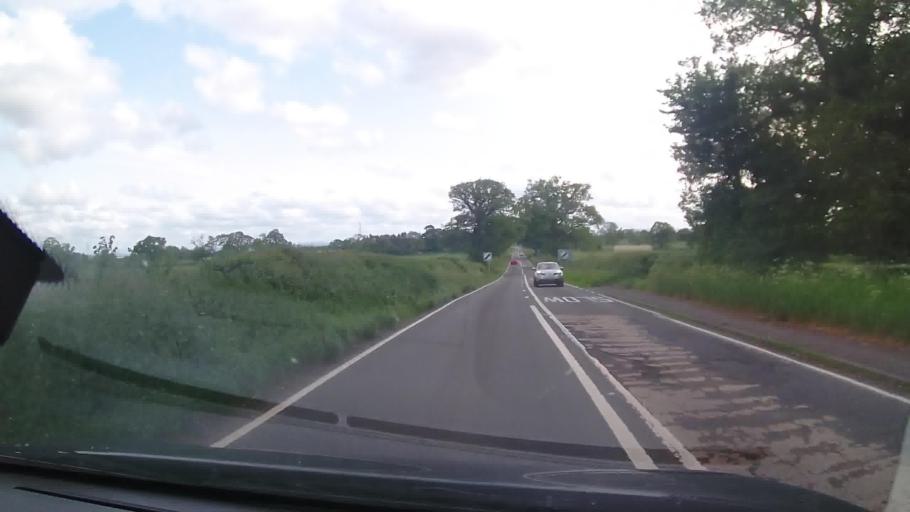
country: GB
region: England
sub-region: Shropshire
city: Astley
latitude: 52.7562
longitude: -2.7448
